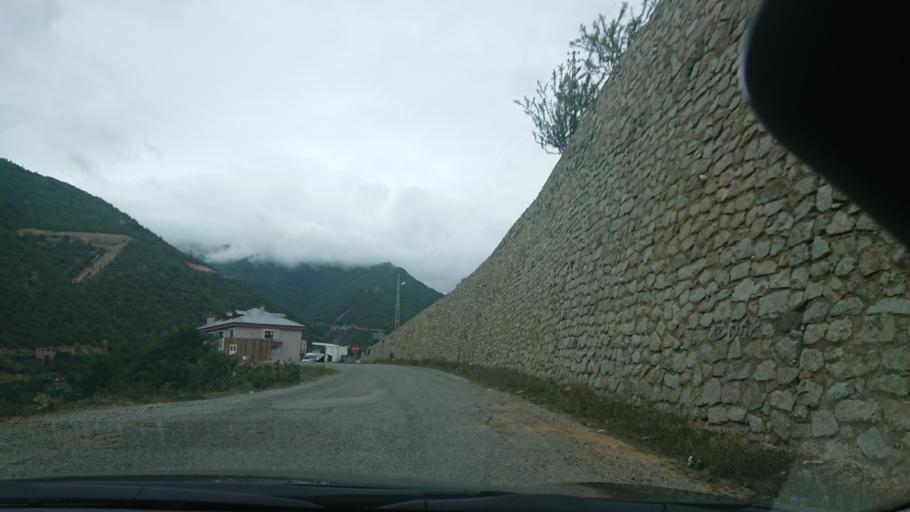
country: TR
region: Gumushane
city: Kurtun
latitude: 40.7036
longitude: 39.0814
